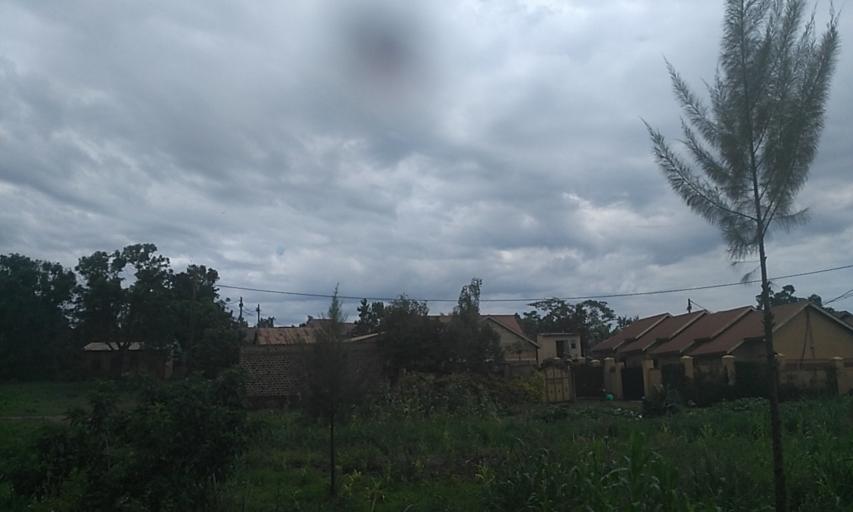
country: UG
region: Central Region
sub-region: Wakiso District
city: Bweyogerere
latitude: 0.3970
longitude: 32.6762
